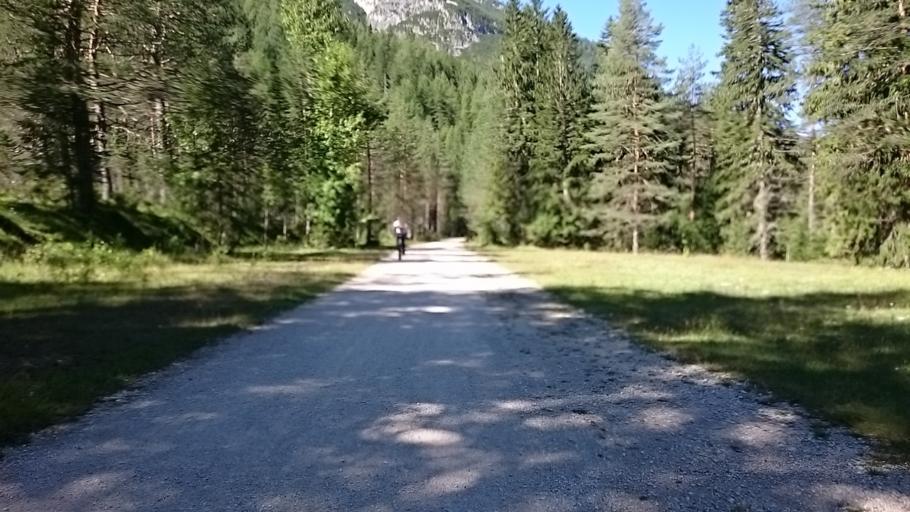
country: IT
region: Veneto
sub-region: Provincia di Belluno
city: Cortina d'Ampezzo
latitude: 46.6167
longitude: 12.2164
